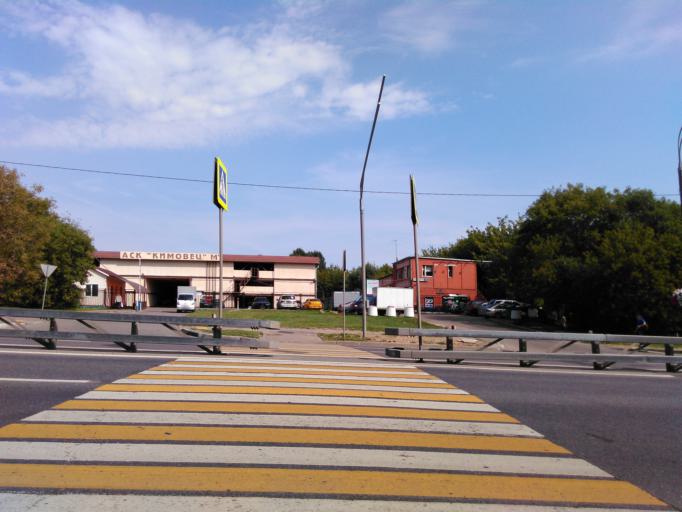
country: RU
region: Moskovskaya
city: Bol'shaya Setun'
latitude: 55.7172
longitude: 37.4233
